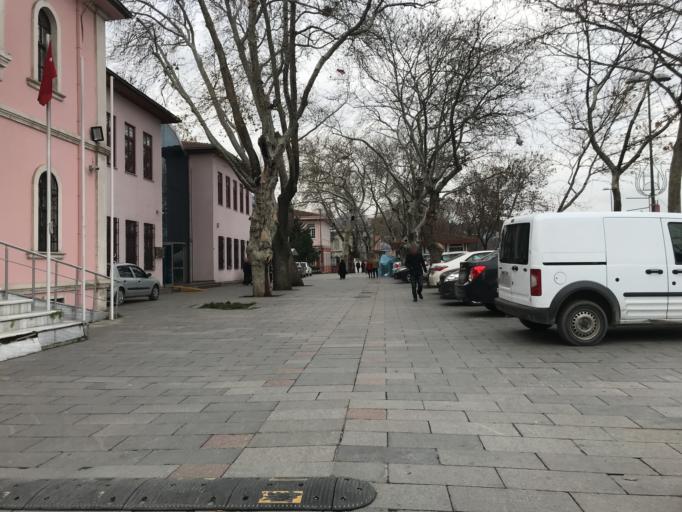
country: TR
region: Istanbul
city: Istanbul
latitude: 41.0432
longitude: 28.9371
